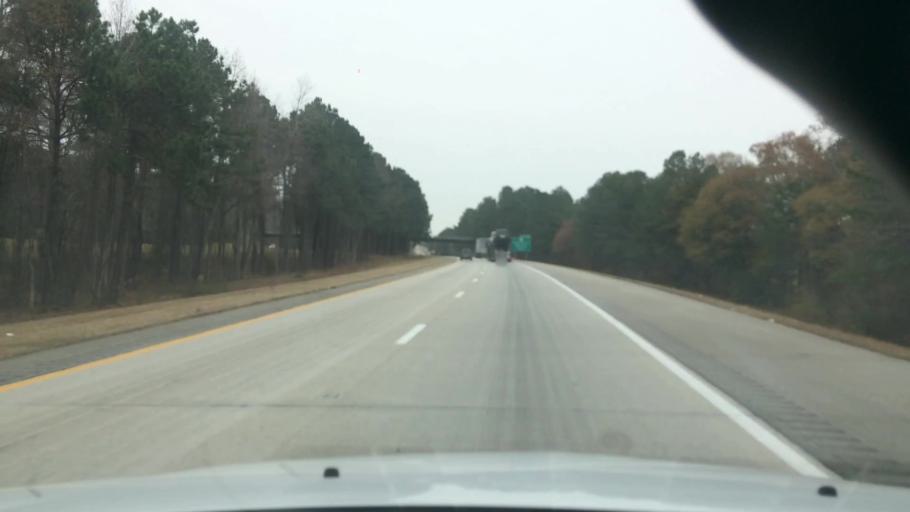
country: US
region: North Carolina
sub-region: Nash County
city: Nashville
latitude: 35.9421
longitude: -77.8939
